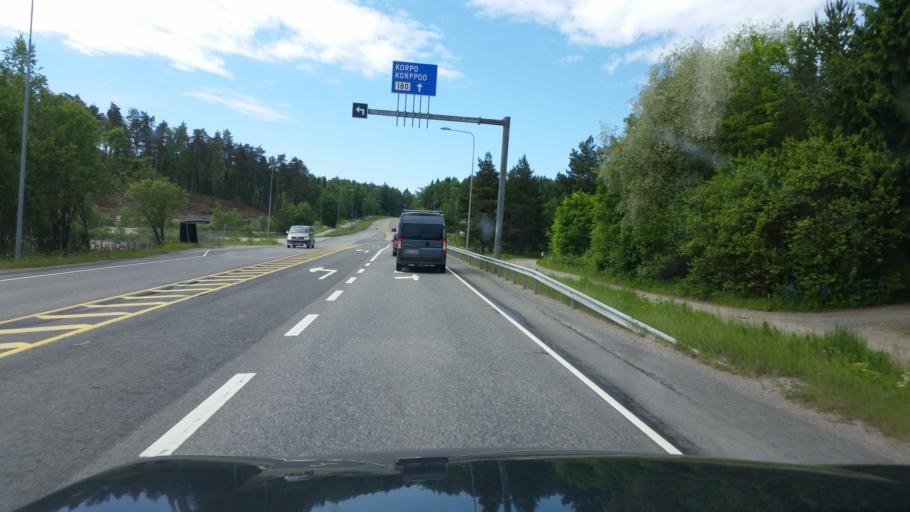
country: FI
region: Varsinais-Suomi
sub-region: Aboland-Turunmaa
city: Pargas
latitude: 60.3211
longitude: 22.3402
